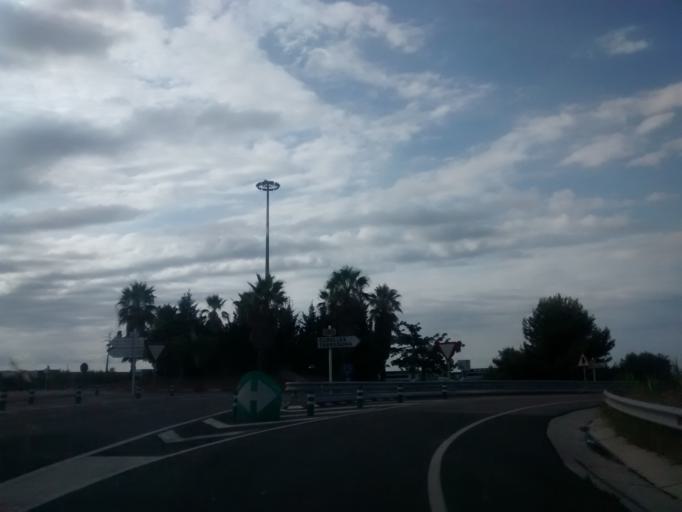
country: ES
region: Catalonia
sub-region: Provincia de Barcelona
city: Vilanova i la Geltru
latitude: 41.2381
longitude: 1.7333
